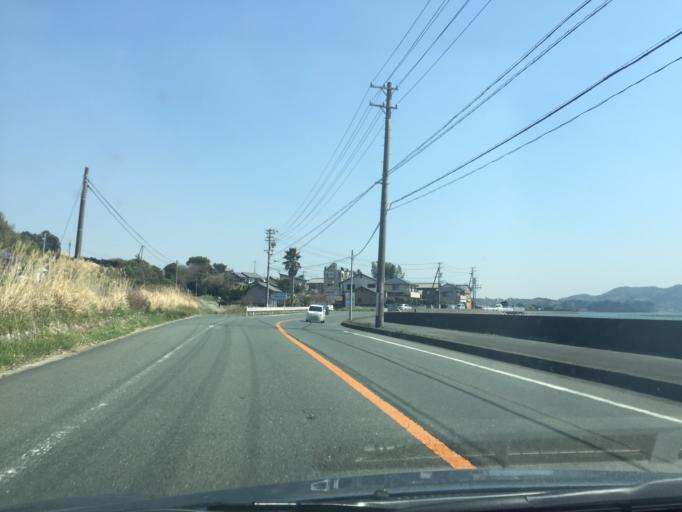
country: JP
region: Shizuoka
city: Kosai-shi
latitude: 34.8021
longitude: 137.6252
